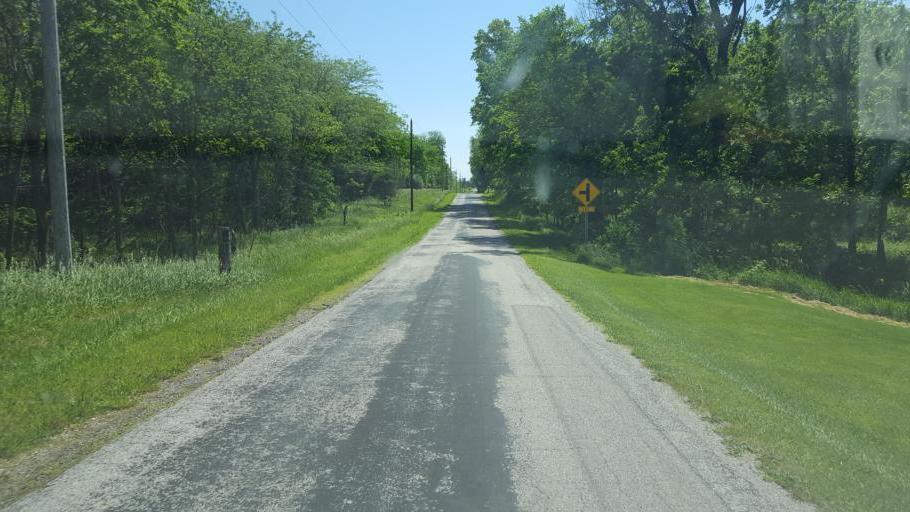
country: US
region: Ohio
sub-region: Hardin County
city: Forest
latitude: 40.6508
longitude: -83.3931
